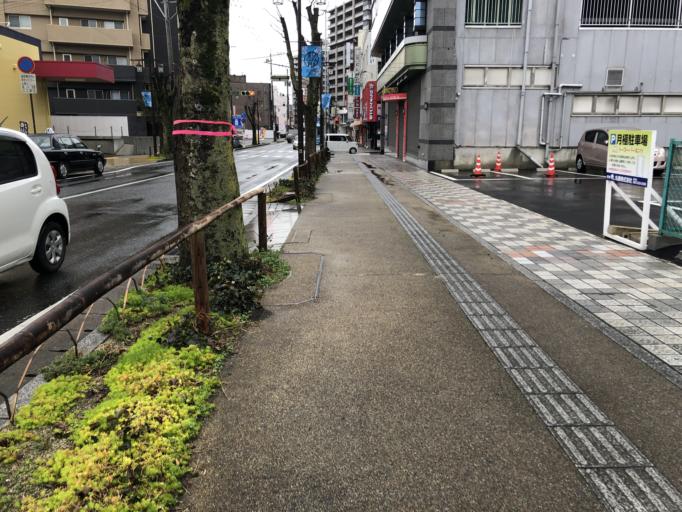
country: JP
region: Oita
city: Hita
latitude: 33.3174
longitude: 130.9375
